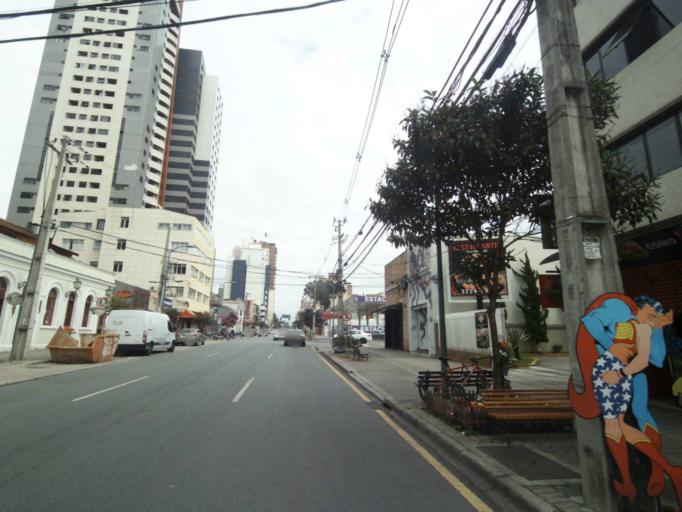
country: BR
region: Parana
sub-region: Curitiba
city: Curitiba
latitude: -25.4333
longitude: -49.2806
